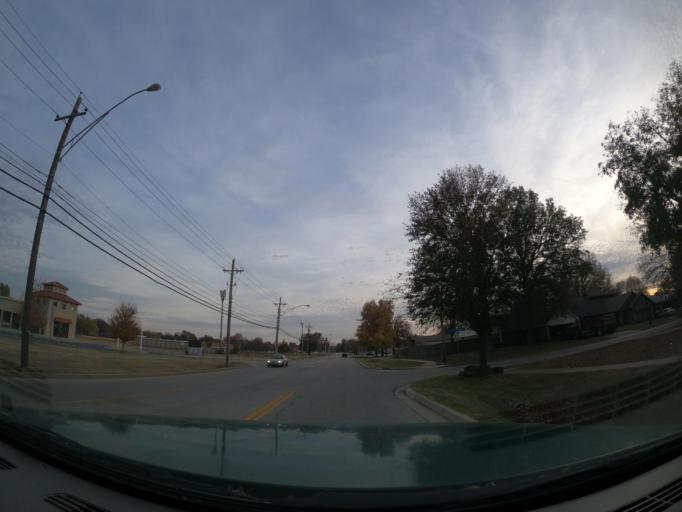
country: US
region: Oklahoma
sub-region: Tulsa County
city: Broken Arrow
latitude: 35.9771
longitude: -95.7974
